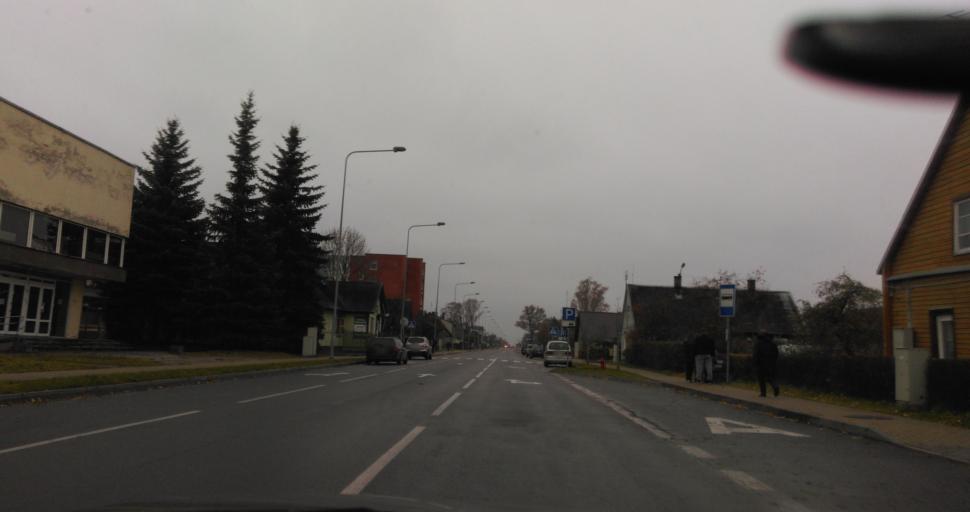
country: LT
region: Panevezys
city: Rokiskis
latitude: 55.9602
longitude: 25.5871
